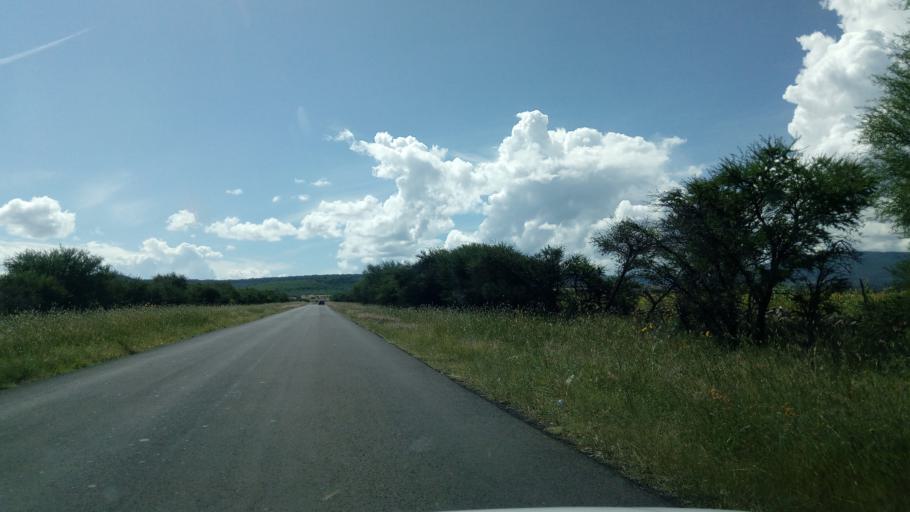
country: MX
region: Durango
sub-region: Durango
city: Jose Refugio Salcido
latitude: 23.8582
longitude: -104.4742
